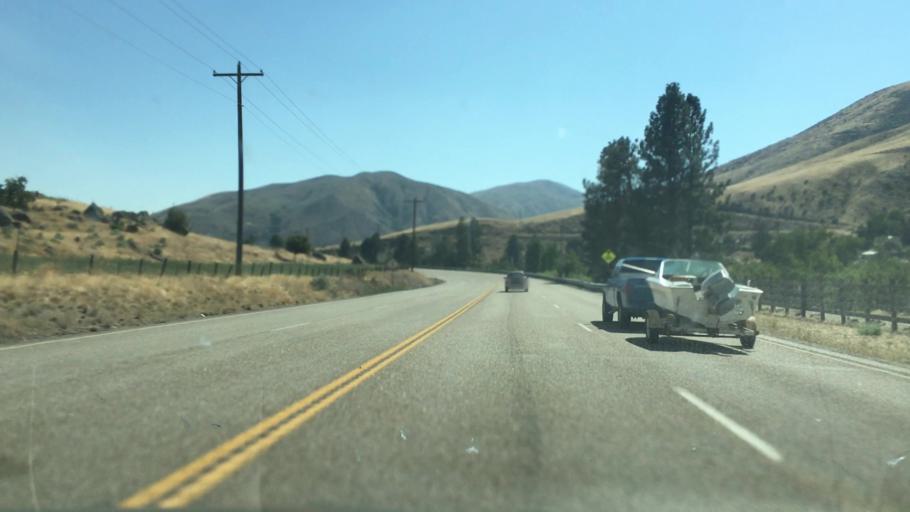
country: US
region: Idaho
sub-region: Gem County
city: Emmett
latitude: 43.9959
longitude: -116.1858
